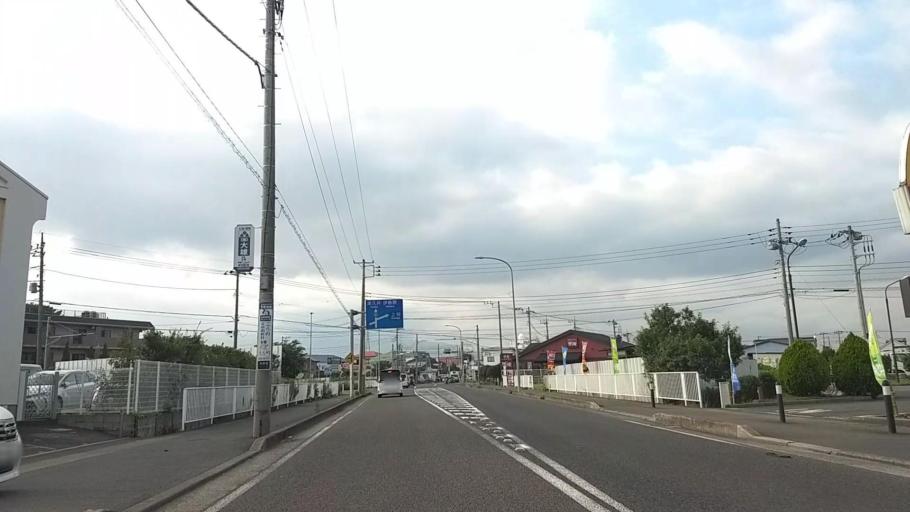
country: JP
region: Kanagawa
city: Hiratsuka
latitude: 35.3546
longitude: 139.3282
